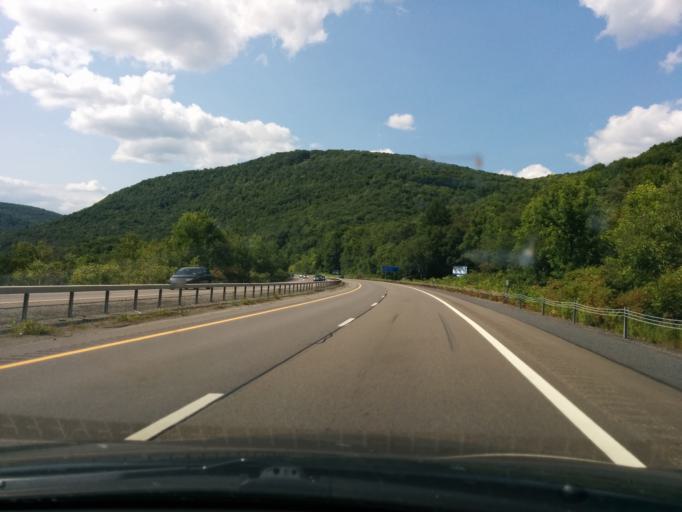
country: US
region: New York
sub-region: Delaware County
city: Hancock
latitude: 41.9601
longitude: -75.2452
